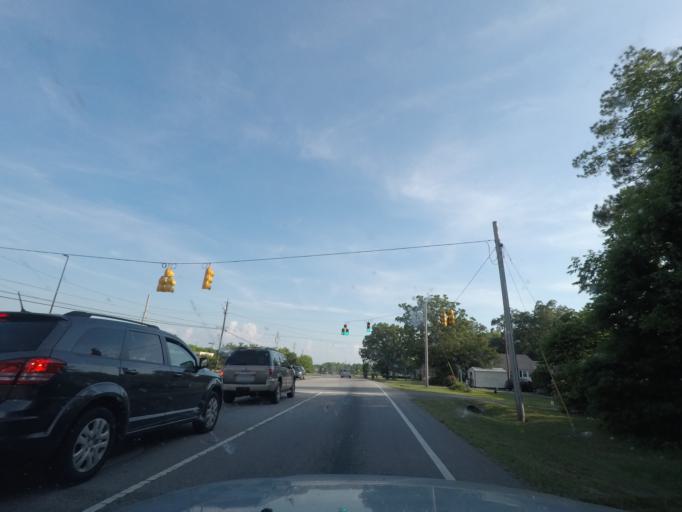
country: US
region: North Carolina
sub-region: Granville County
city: Oxford
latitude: 36.2813
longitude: -78.6068
